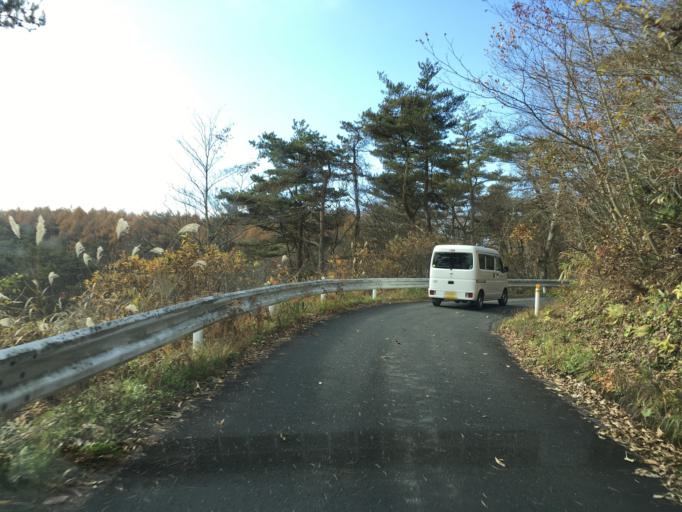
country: JP
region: Iwate
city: Mizusawa
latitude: 39.1234
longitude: 141.3049
